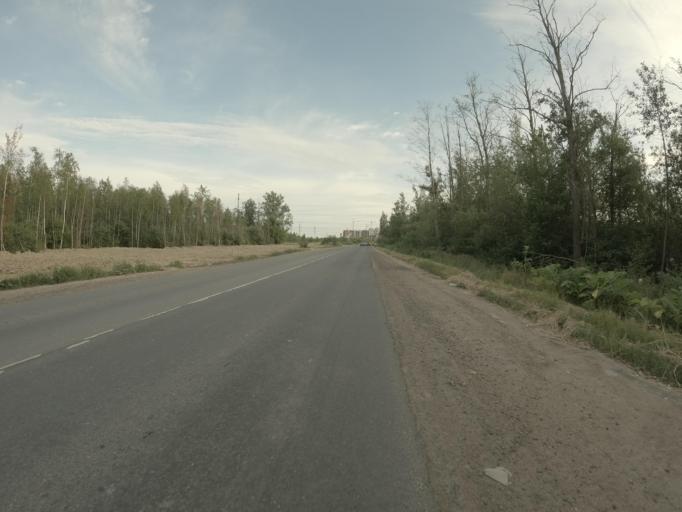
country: RU
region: St.-Petersburg
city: Krasnogvargeisky
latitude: 59.9279
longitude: 30.5203
